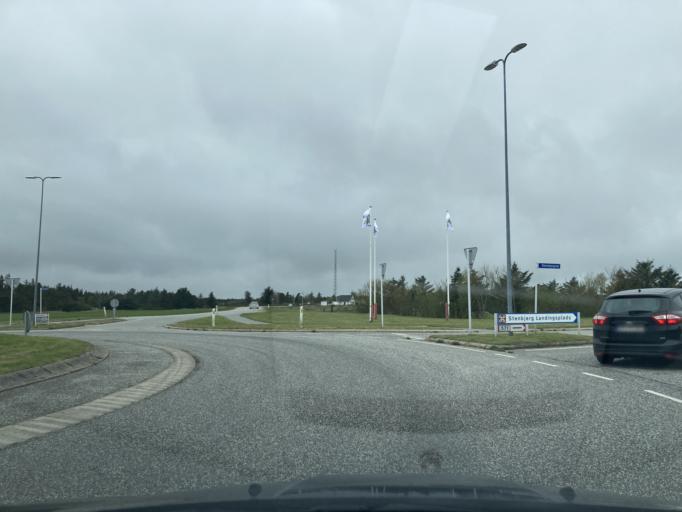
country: DK
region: North Denmark
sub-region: Thisted Kommune
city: Hurup
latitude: 56.9197
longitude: 8.3728
